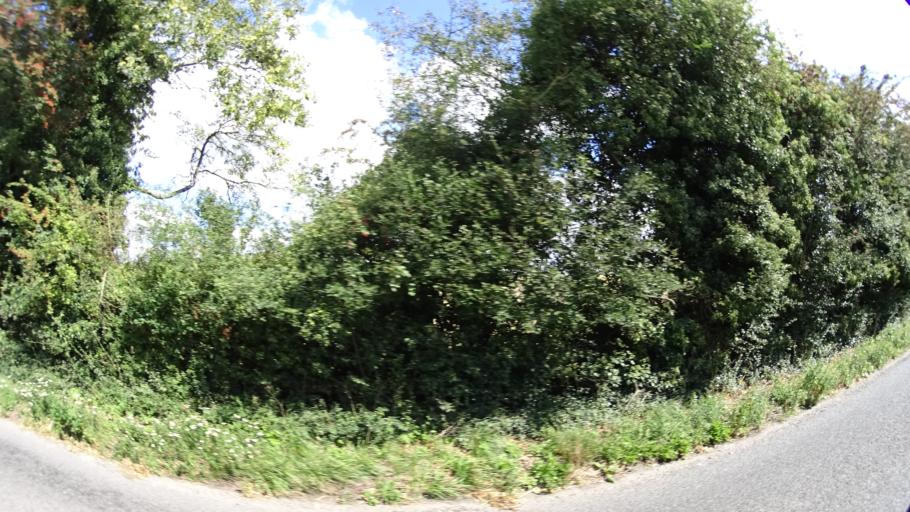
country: GB
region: England
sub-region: Wiltshire
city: Tidworth
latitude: 51.1784
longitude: -1.6465
